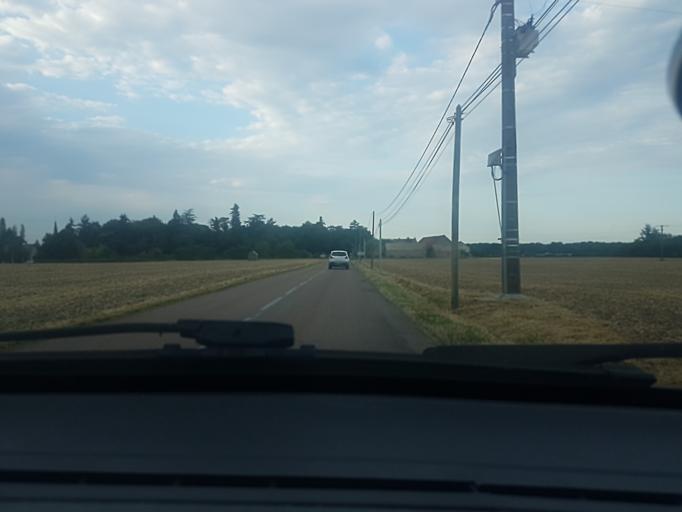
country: FR
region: Bourgogne
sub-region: Departement de Saone-et-Loire
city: Buxy
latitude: 46.7055
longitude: 4.7721
